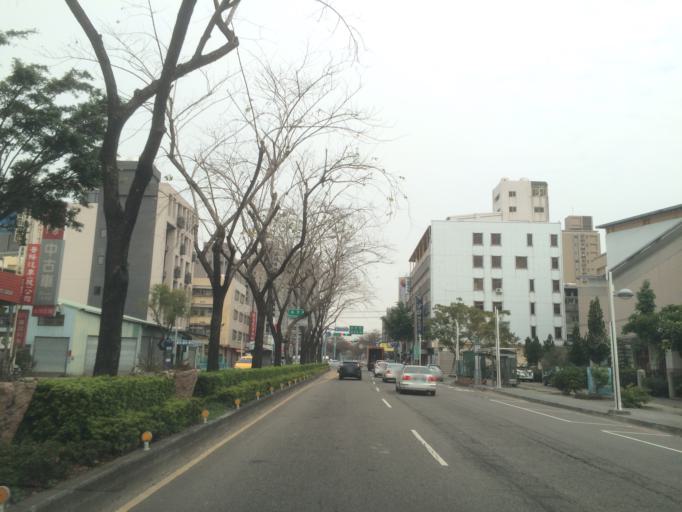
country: TW
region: Taiwan
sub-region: Taichung City
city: Taichung
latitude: 24.1923
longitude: 120.6865
